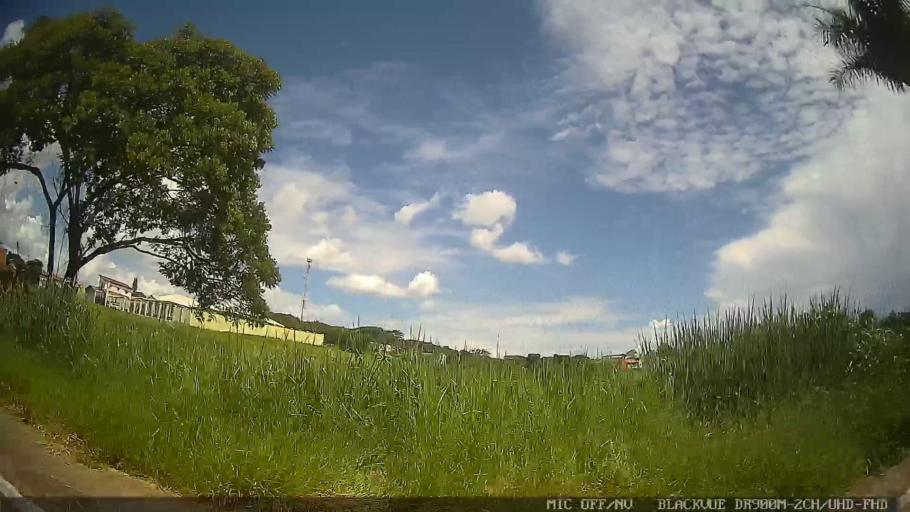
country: BR
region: Sao Paulo
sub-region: Conchas
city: Conchas
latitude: -23.0160
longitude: -48.0168
